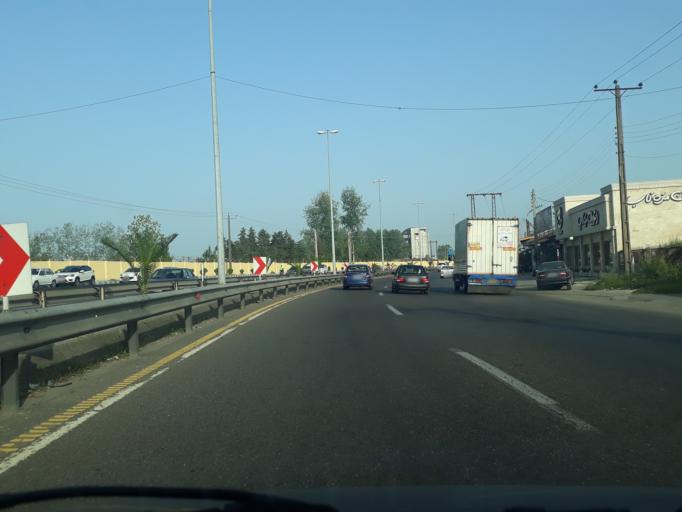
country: IR
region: Gilan
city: Bandar-e Anzali
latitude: 37.4572
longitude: 49.6121
